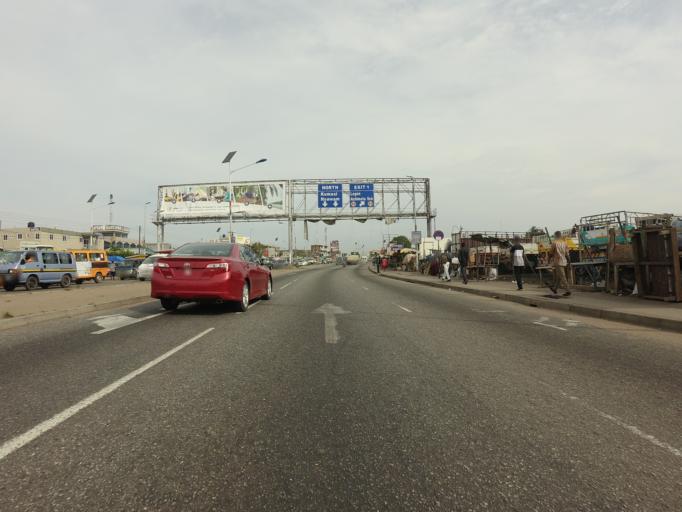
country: GH
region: Greater Accra
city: Dome
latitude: 5.6149
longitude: -0.2292
